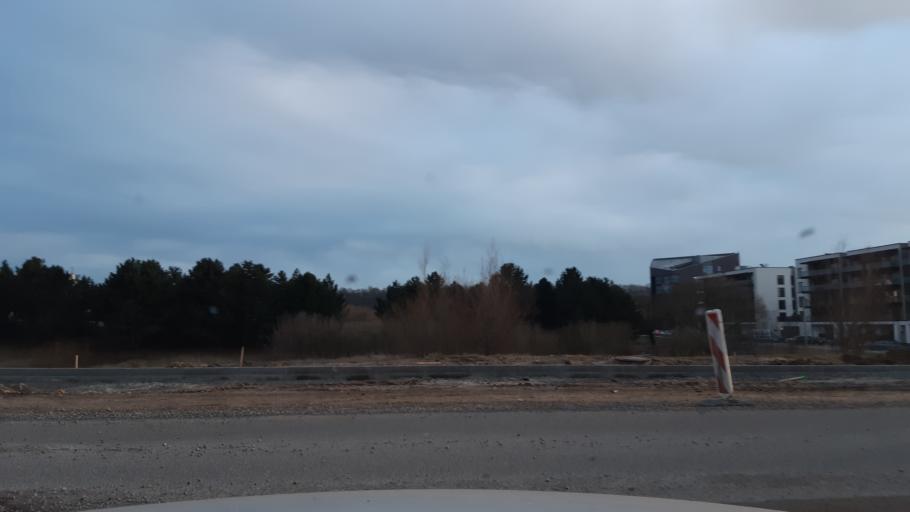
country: LT
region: Kauno apskritis
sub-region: Kaunas
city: Kaunas
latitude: 54.9030
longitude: 23.8822
